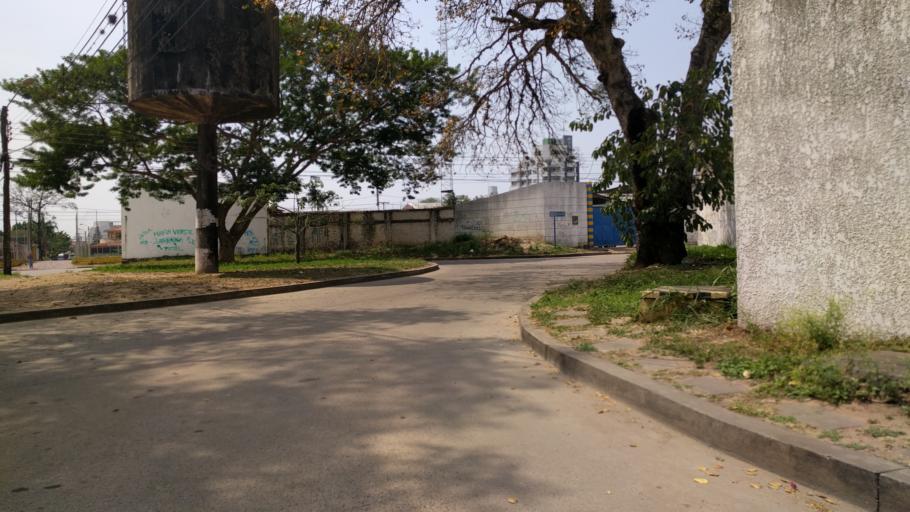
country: BO
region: Santa Cruz
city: Santa Cruz de la Sierra
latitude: -17.8098
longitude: -63.2085
